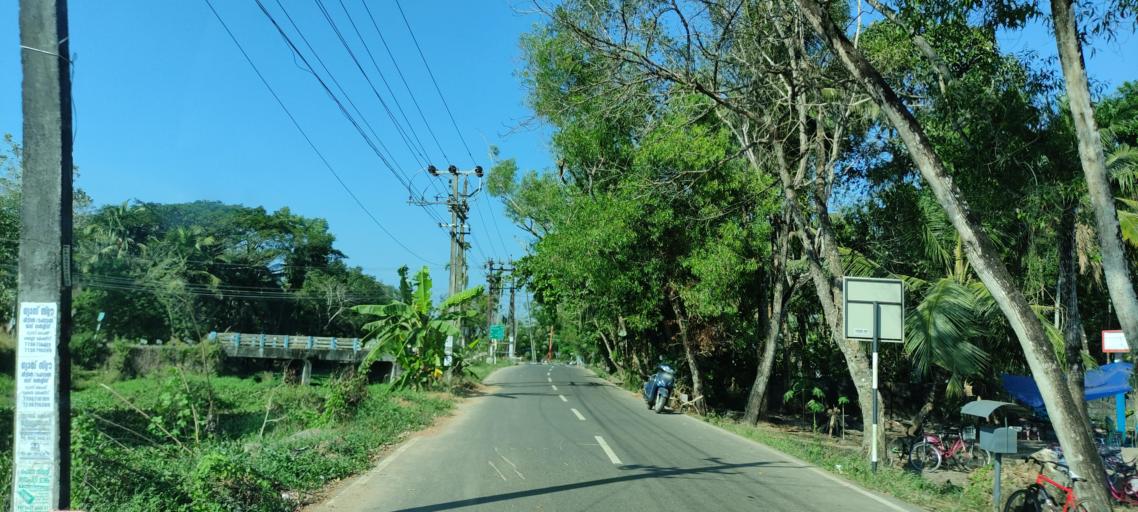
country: IN
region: Kerala
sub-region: Alappuzha
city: Alleppey
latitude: 9.5703
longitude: 76.3307
